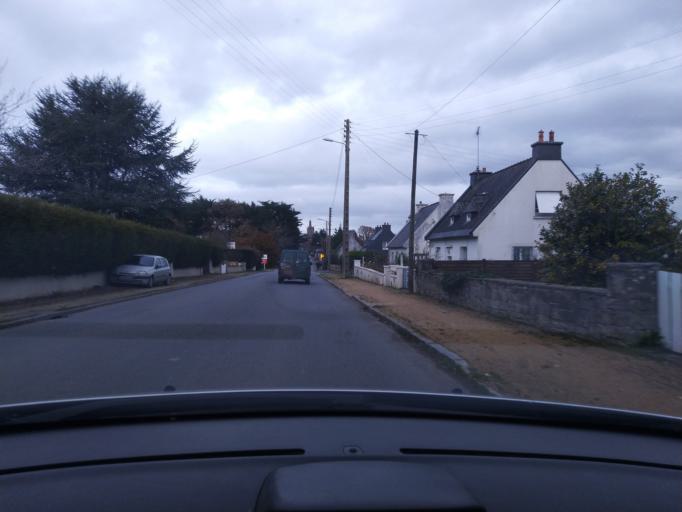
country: FR
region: Brittany
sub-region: Departement des Cotes-d'Armor
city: Plouaret
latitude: 48.6080
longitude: -3.4783
